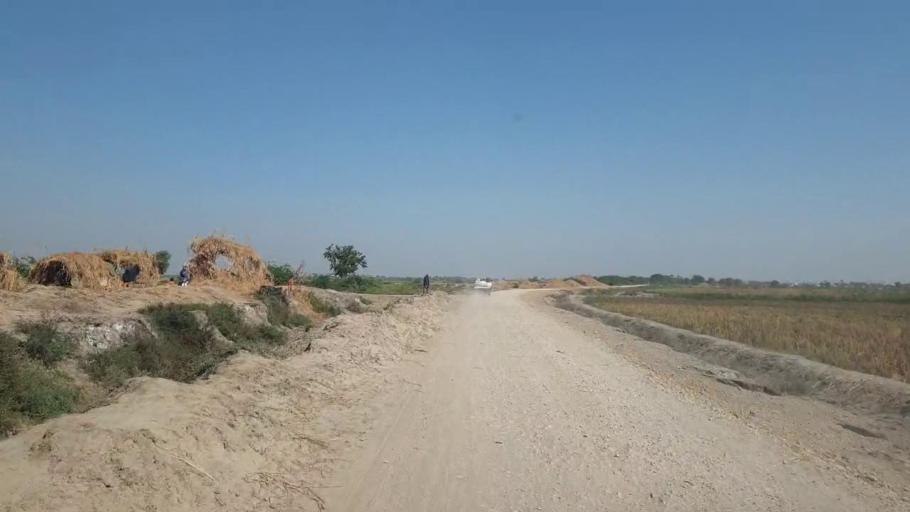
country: PK
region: Sindh
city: Talhar
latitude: 24.7835
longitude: 68.7867
